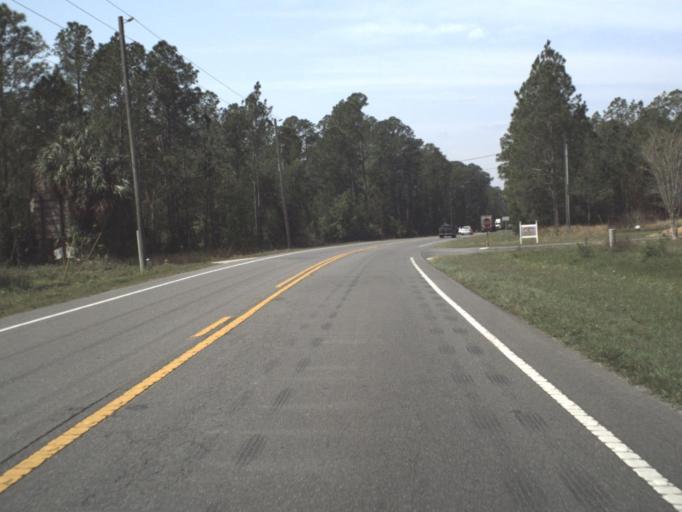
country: US
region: Florida
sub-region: Lake County
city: Astor
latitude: 29.1577
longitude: -81.5580
